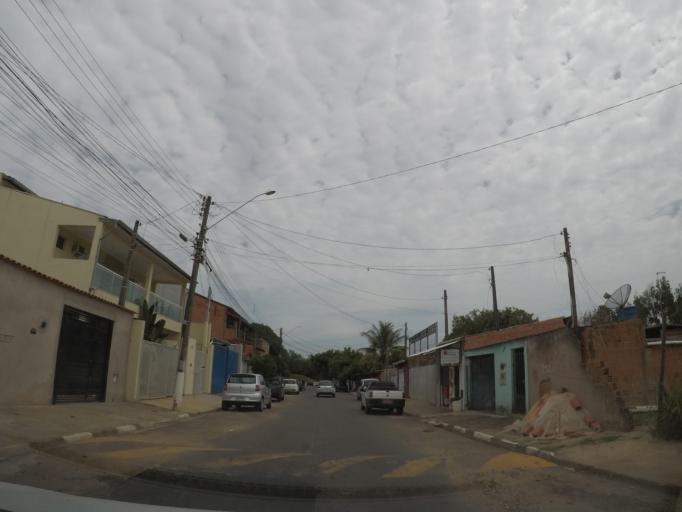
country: BR
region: Sao Paulo
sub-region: Hortolandia
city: Hortolandia
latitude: -22.8358
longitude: -47.2055
